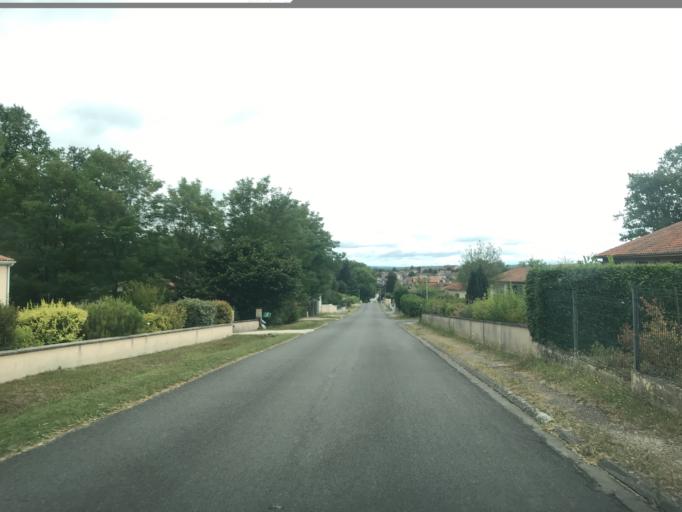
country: FR
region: Poitou-Charentes
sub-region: Departement de la Charente
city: Dignac
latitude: 45.5523
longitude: 0.2725
